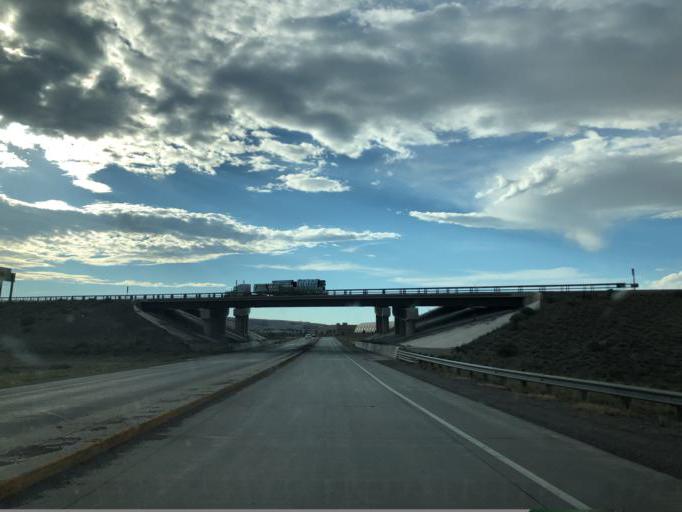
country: US
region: Wyoming
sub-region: Carbon County
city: Rawlins
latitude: 41.7884
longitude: -107.1993
